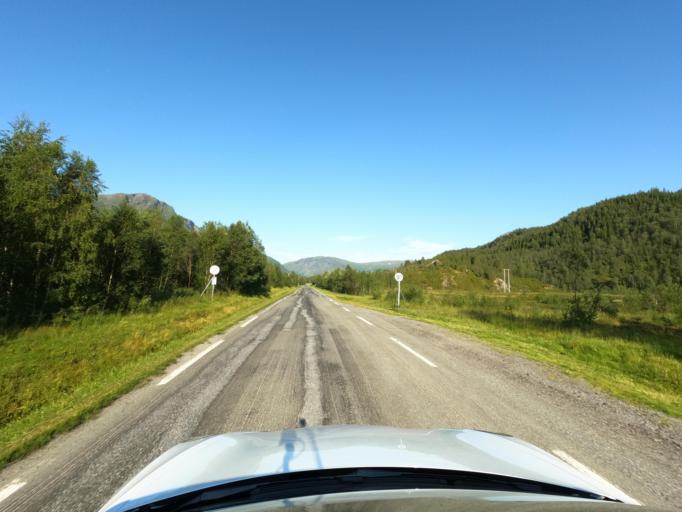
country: NO
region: Nordland
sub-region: Narvik
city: Bjerkvik
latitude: 68.5578
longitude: 17.6301
